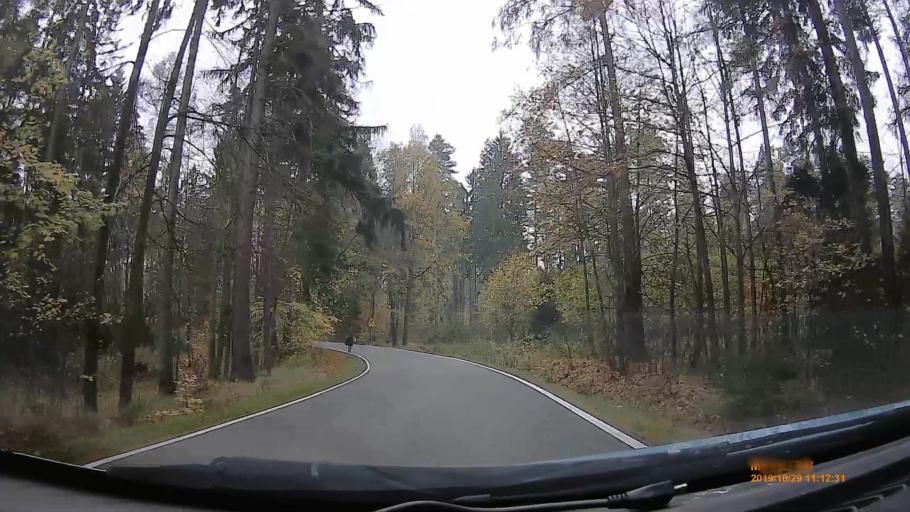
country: PL
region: Lower Silesian Voivodeship
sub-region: Powiat klodzki
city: Polanica-Zdroj
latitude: 50.4263
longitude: 16.5050
